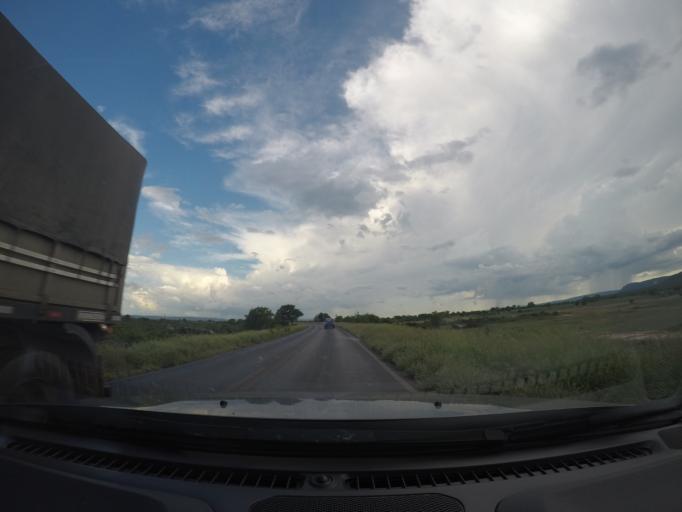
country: BR
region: Bahia
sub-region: Ibotirama
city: Ibotirama
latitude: -12.1508
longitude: -43.3121
